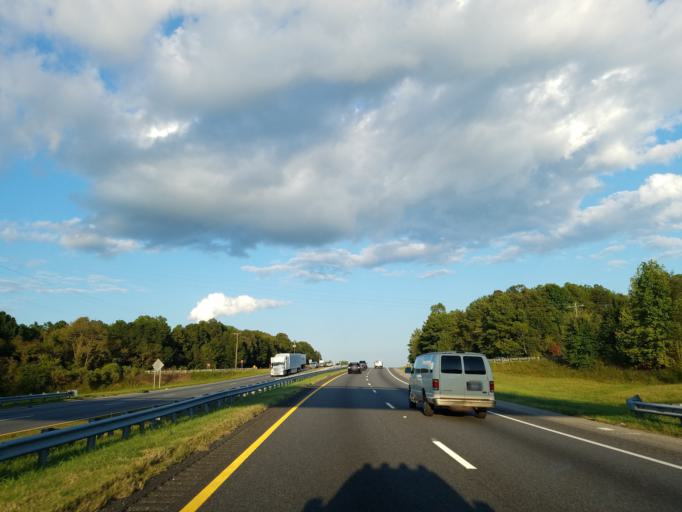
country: US
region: South Carolina
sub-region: Cherokee County
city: East Gaffney
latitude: 35.1099
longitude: -81.6025
